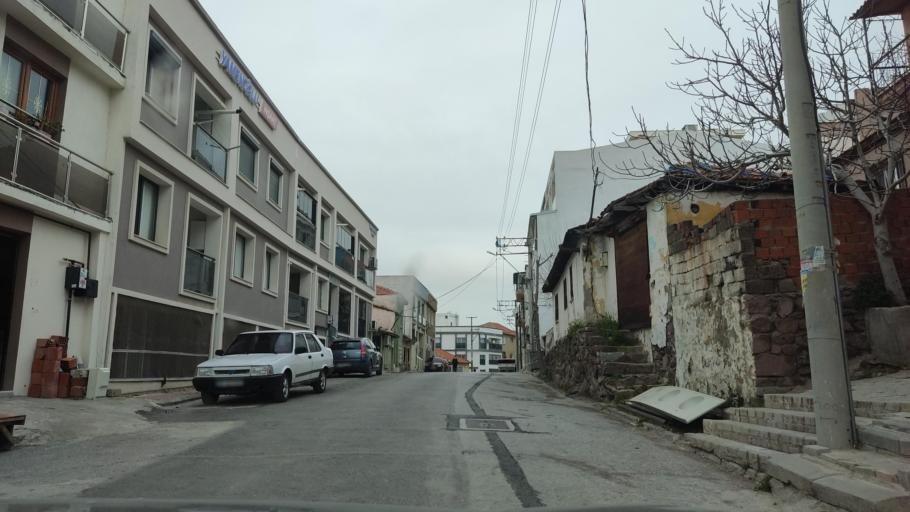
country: TR
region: Izmir
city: Karsiyaka
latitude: 38.4921
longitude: 27.0682
